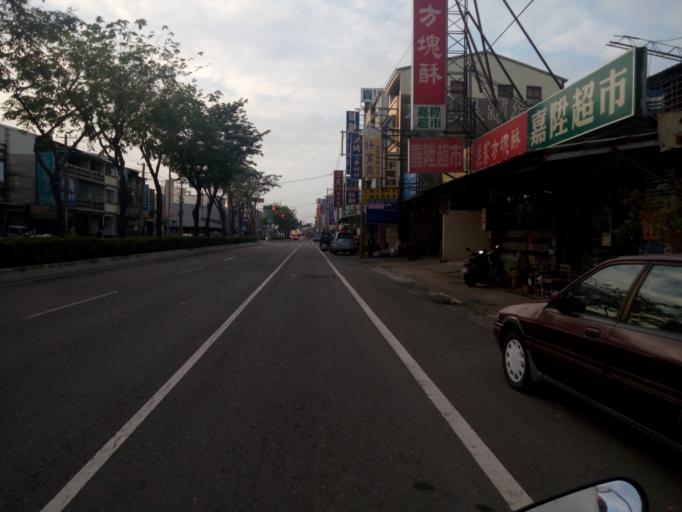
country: TW
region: Taiwan
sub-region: Chiayi
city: Jiayi Shi
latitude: 23.4829
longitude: 120.4256
